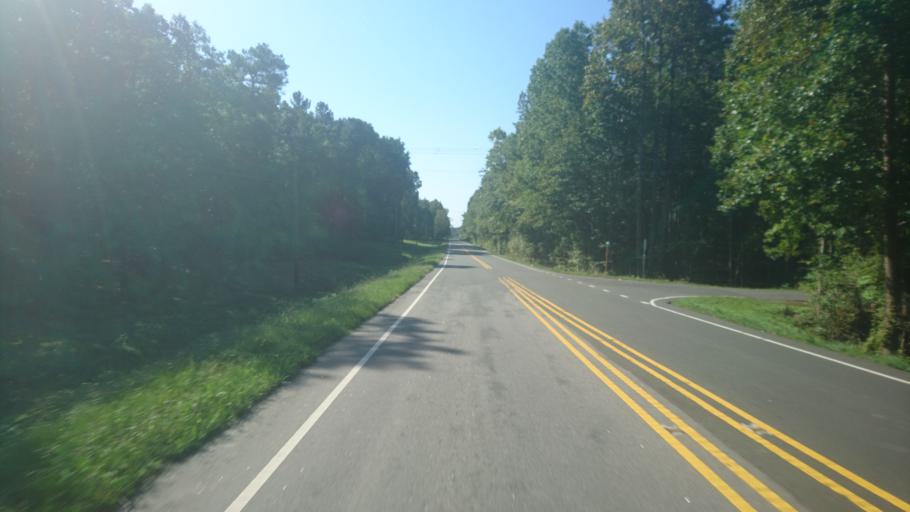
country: US
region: North Carolina
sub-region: Orange County
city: Hillsborough
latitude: 36.0355
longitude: -79.0816
